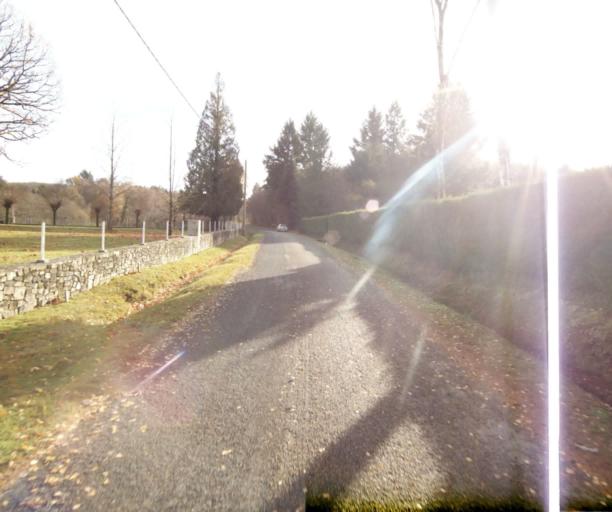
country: FR
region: Limousin
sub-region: Departement de la Correze
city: Sainte-Fortunade
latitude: 45.1952
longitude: 1.7358
